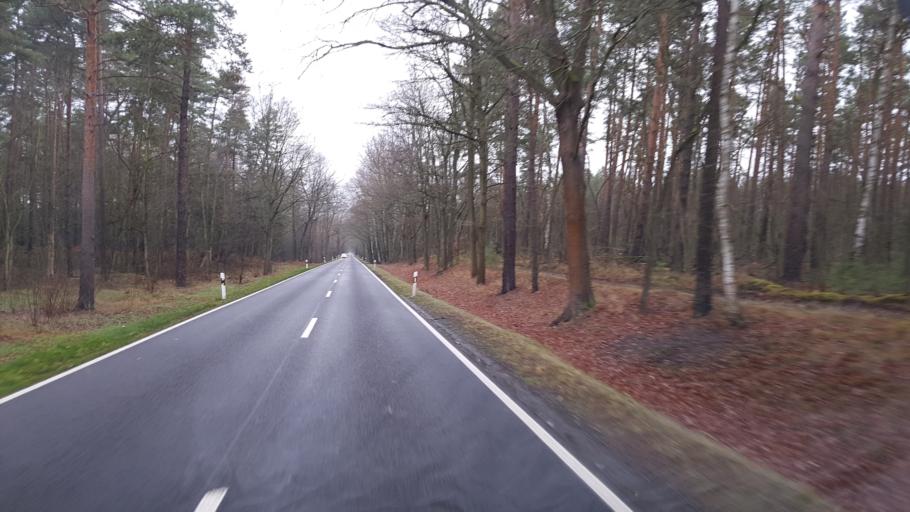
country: DE
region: Brandenburg
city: Altdobern
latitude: 51.7061
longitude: 14.0241
